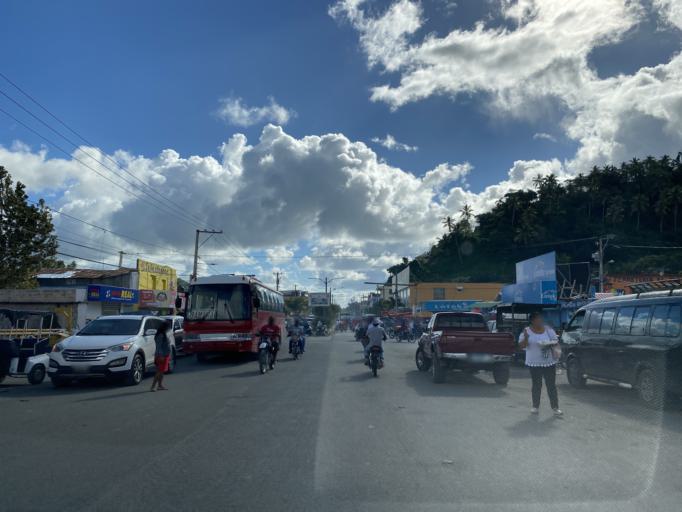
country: DO
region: Samana
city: Samana
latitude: 19.2047
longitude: -69.3435
